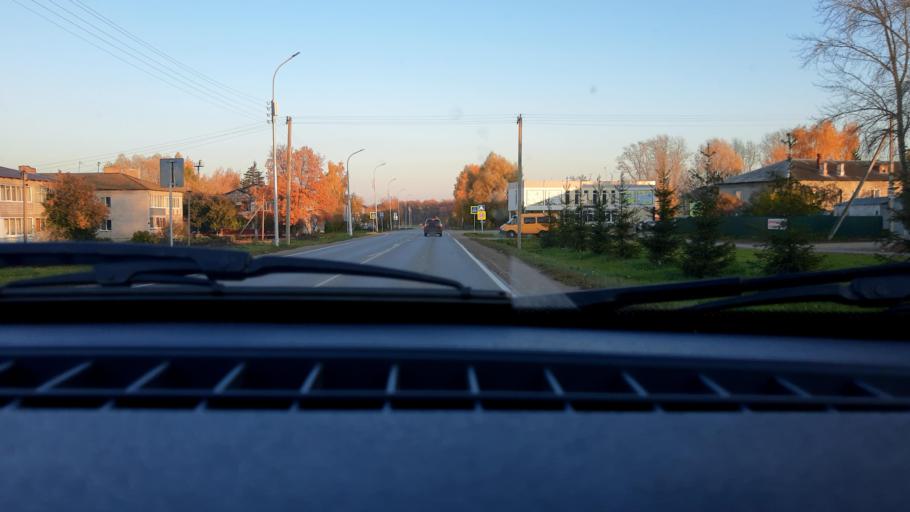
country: RU
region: Bashkortostan
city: Mikhaylovka
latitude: 54.8118
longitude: 55.8071
